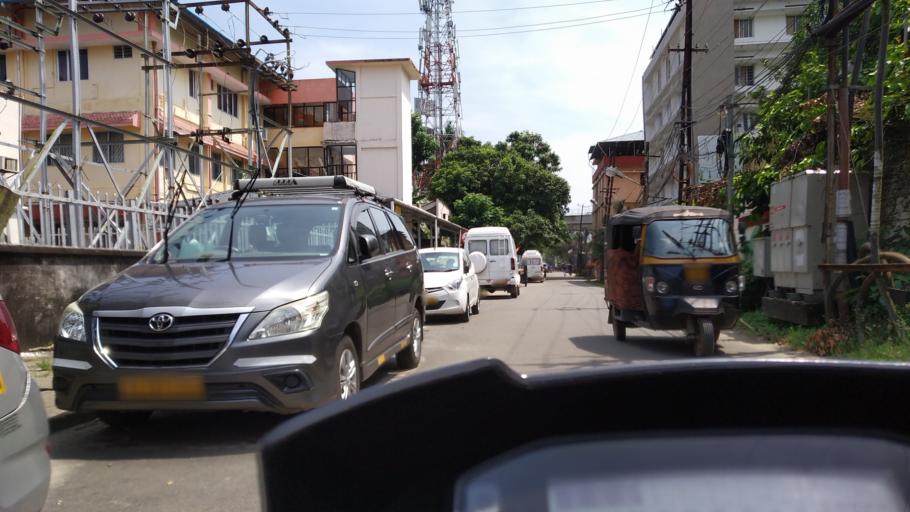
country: IN
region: Kerala
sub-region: Ernakulam
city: Cochin
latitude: 9.9702
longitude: 76.2900
